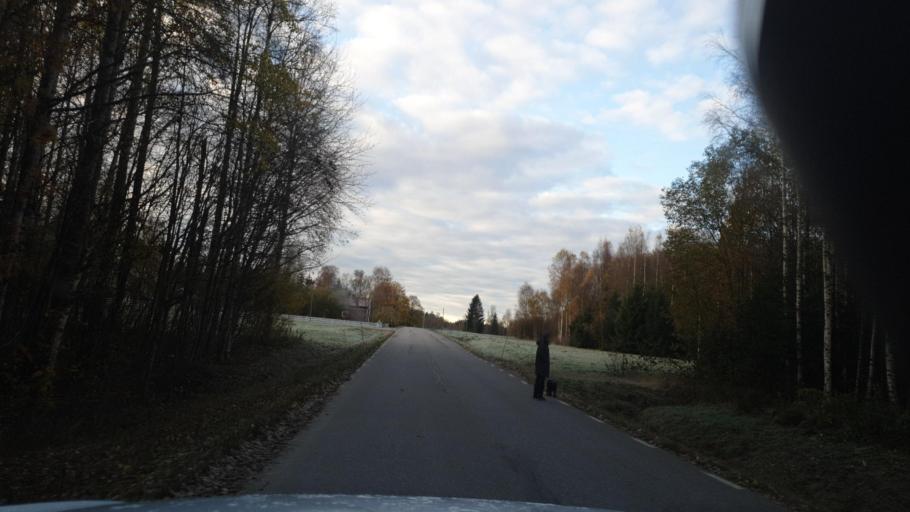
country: SE
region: Vaermland
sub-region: Eda Kommun
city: Amotfors
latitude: 59.7226
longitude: 12.1619
